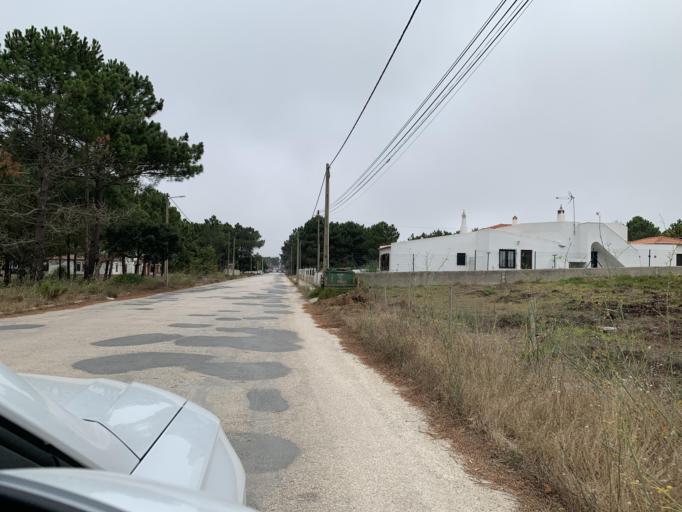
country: PT
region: Faro
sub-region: Aljezur
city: Aljezur
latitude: 37.3093
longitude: -8.8531
